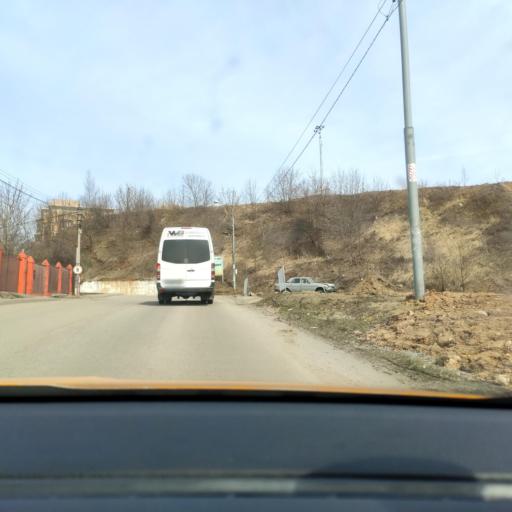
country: RU
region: Moskovskaya
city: Skhodnya
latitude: 55.9403
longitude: 37.3193
